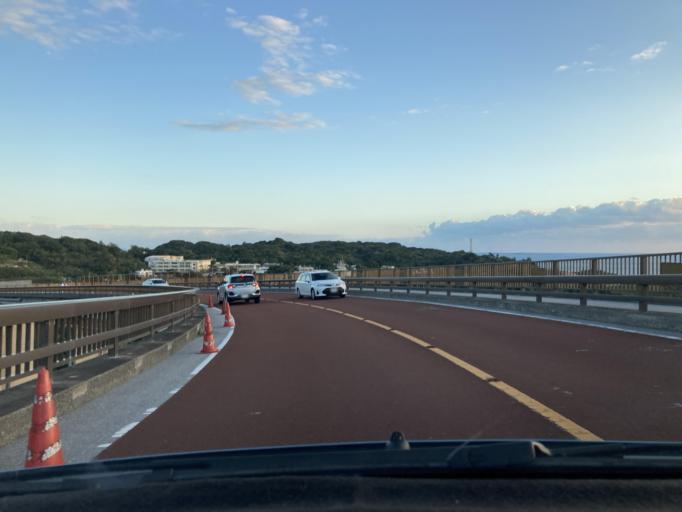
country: JP
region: Okinawa
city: Ginowan
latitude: 26.1647
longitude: 127.8176
